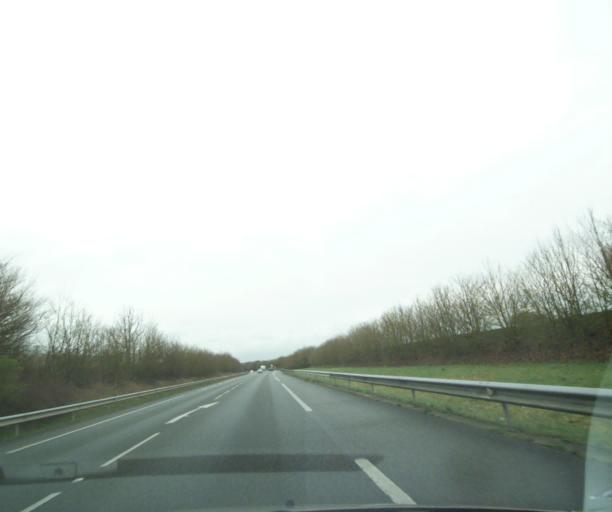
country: FR
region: Picardie
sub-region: Departement de l'Oise
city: Noyon
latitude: 49.5718
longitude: 3.0271
